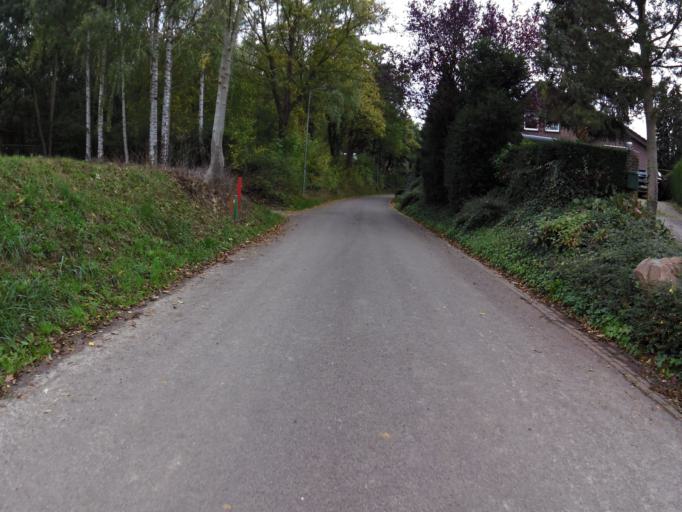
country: NL
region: Limburg
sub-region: Gemeente Voerendaal
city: Kunrade
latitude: 50.8727
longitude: 5.9461
